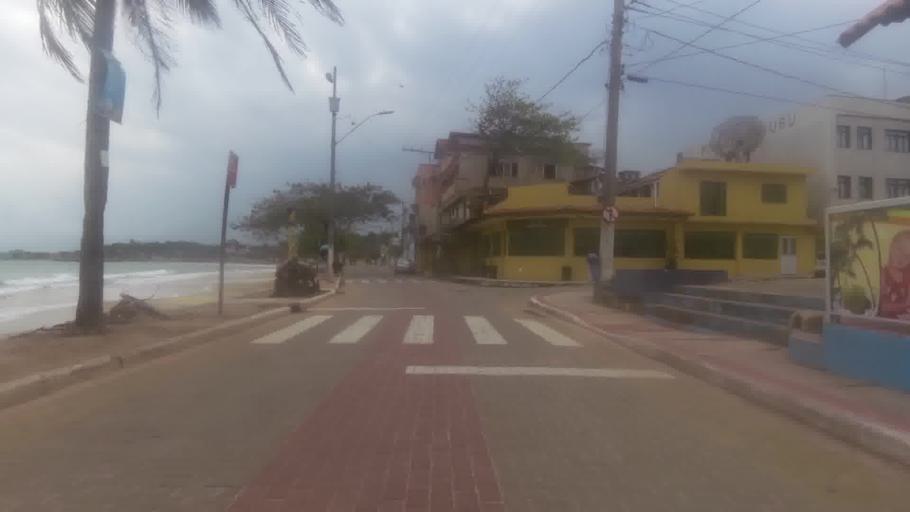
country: BR
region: Espirito Santo
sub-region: Piuma
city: Piuma
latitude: -20.8021
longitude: -40.5887
